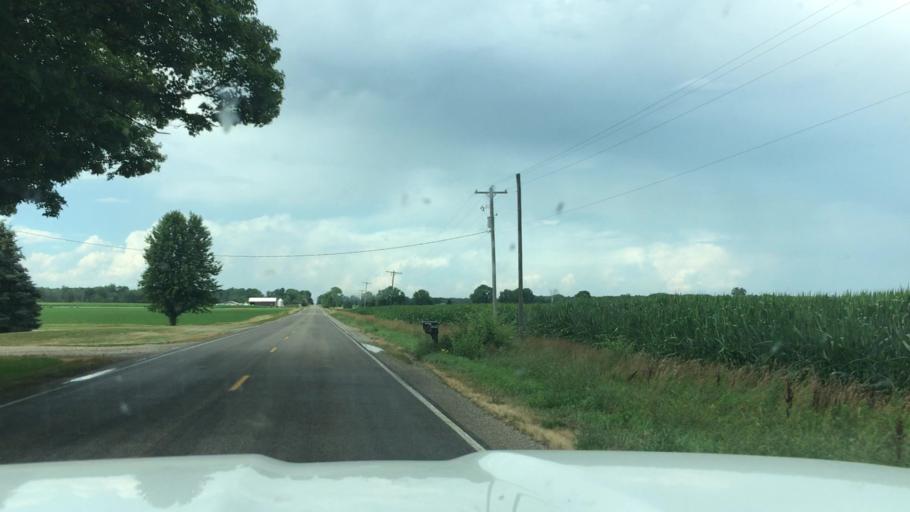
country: US
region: Michigan
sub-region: Montcalm County
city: Carson City
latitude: 43.2250
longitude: -84.7778
